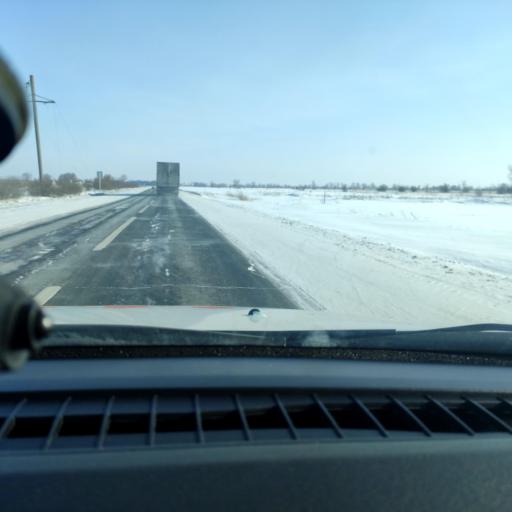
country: RU
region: Samara
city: Smyshlyayevka
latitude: 53.1844
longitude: 50.4844
